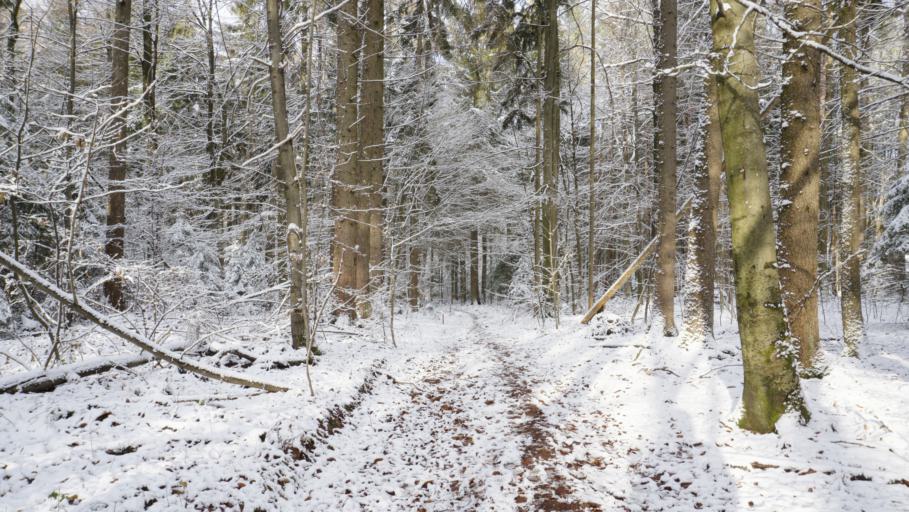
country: DE
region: Baden-Wuerttemberg
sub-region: Karlsruhe Region
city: Neunkirchen
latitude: 49.4064
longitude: 9.0202
